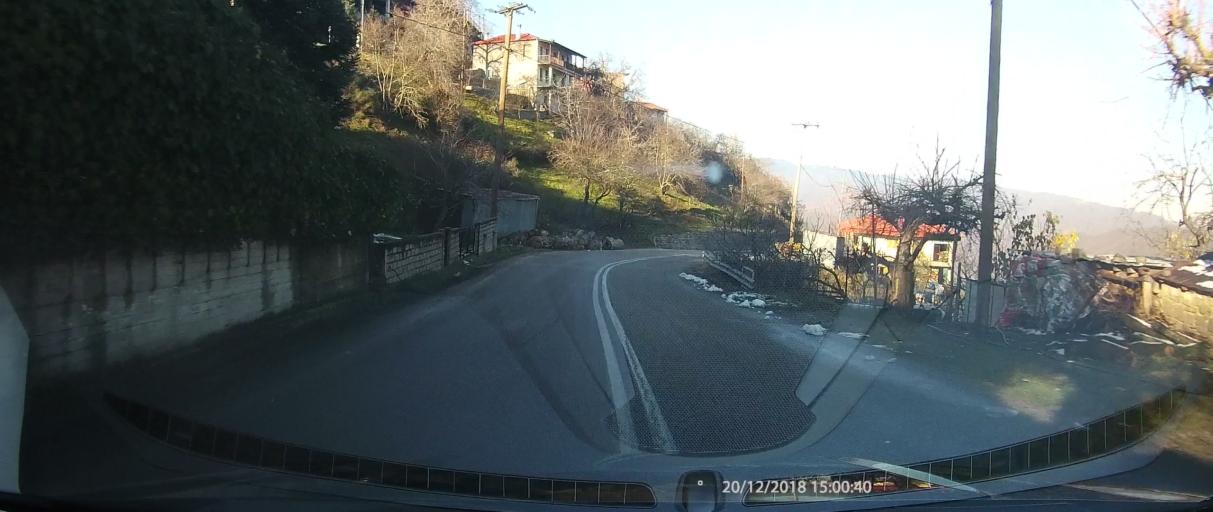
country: GR
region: Central Greece
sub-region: Nomos Evrytanias
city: Karpenisi
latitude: 38.9085
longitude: 21.9171
